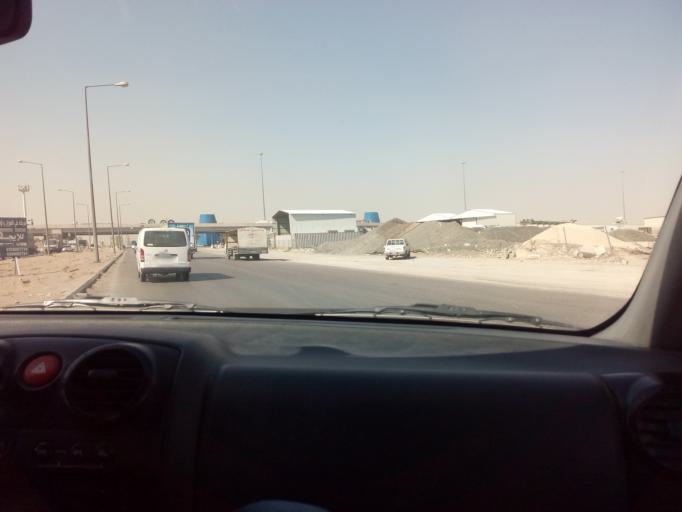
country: SA
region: Ar Riyad
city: Riyadh
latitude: 24.6444
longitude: 46.8418
